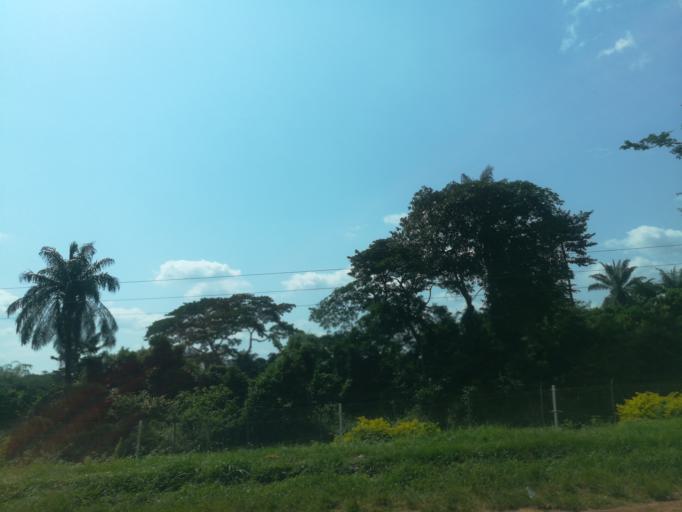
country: NG
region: Oyo
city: Moniya
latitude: 7.5063
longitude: 3.9129
